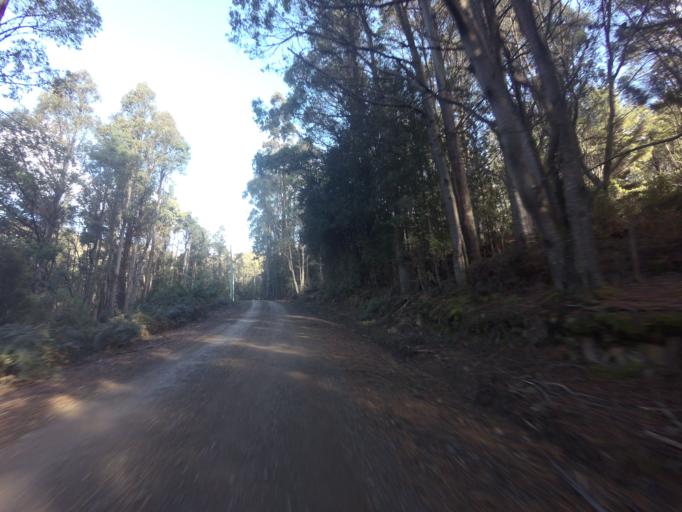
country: AU
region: Tasmania
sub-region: Glenorchy
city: Berriedale
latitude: -42.8570
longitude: 147.1662
